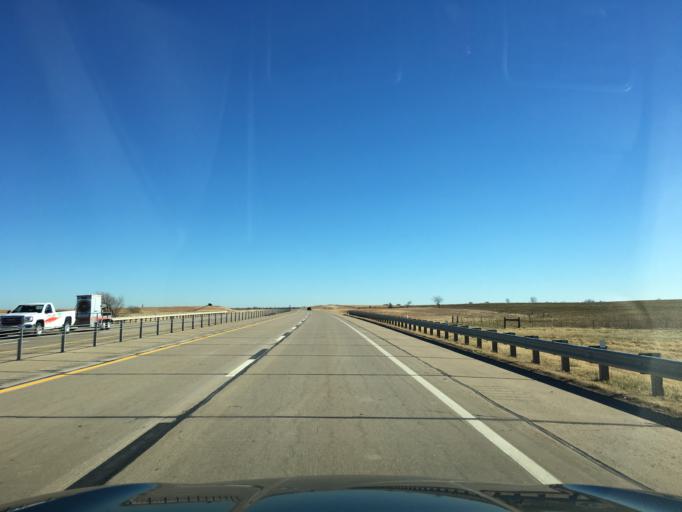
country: US
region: Oklahoma
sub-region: Noble County
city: Perry
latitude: 36.3957
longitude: -97.2246
